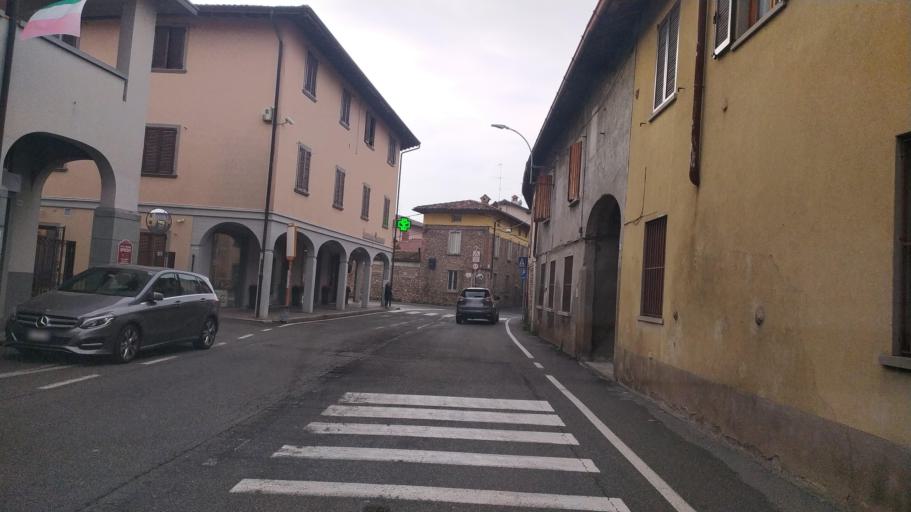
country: IT
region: Lombardy
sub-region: Provincia di Bergamo
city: Lallio
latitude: 45.6785
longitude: 9.6301
